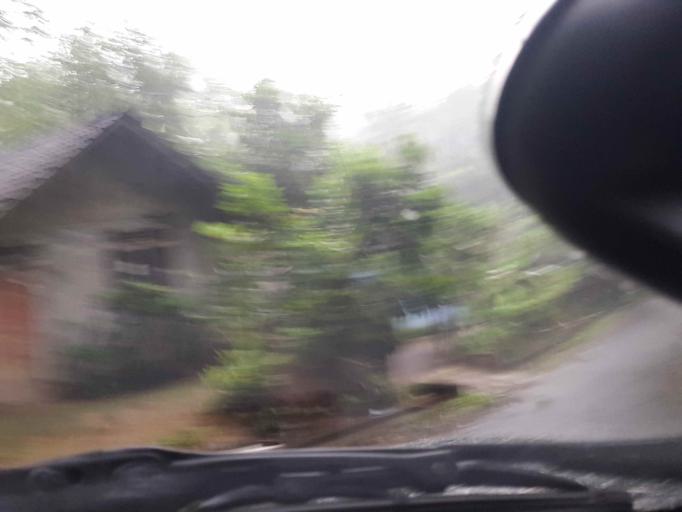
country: ID
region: Central Java
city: Wonosobo
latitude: -7.5038
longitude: 109.9977
